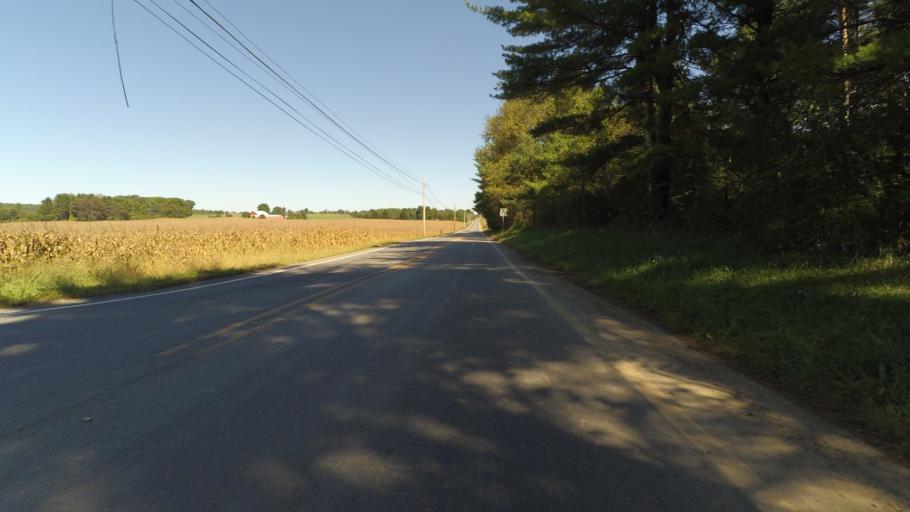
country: US
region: Pennsylvania
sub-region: Centre County
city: Park Forest Village
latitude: 40.7677
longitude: -77.9164
